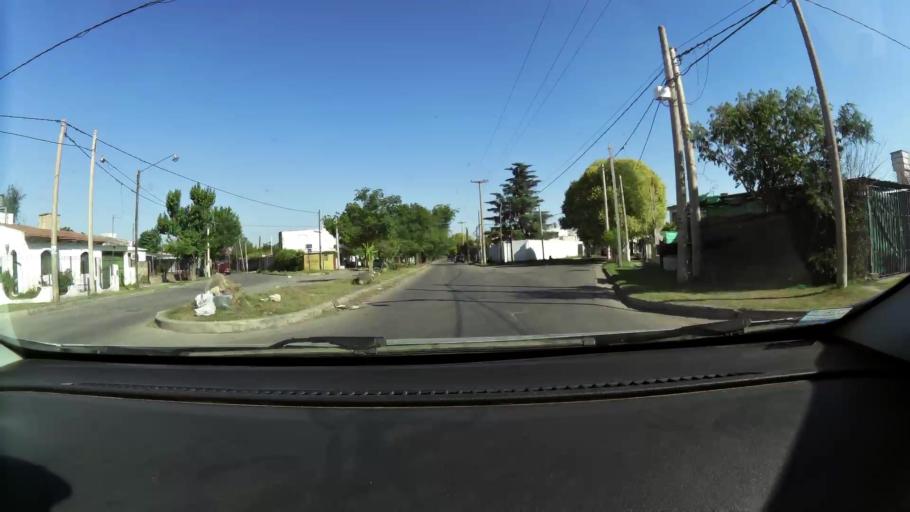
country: AR
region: Cordoba
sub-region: Departamento de Capital
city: Cordoba
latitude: -31.3634
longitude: -64.1915
